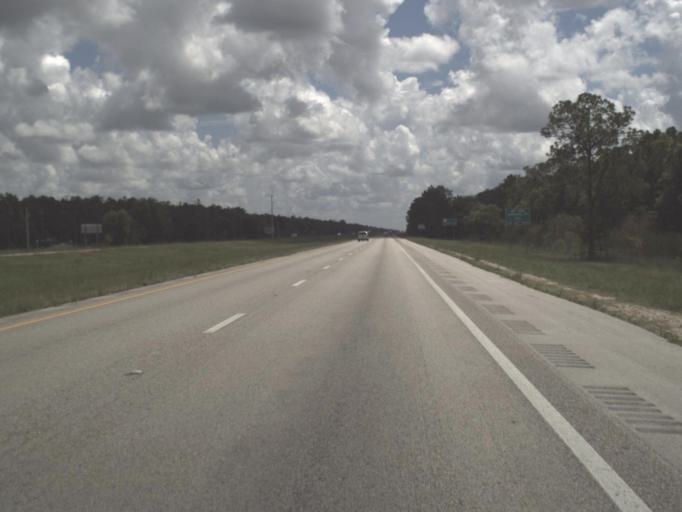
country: US
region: Florida
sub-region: Collier County
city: Golden Gate
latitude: 26.1549
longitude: -81.6613
